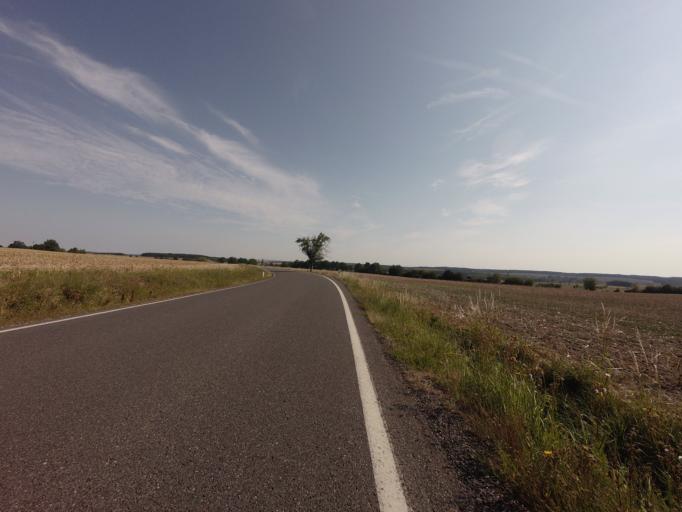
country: CZ
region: Jihocesky
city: Bernartice
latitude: 49.3361
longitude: 14.3637
